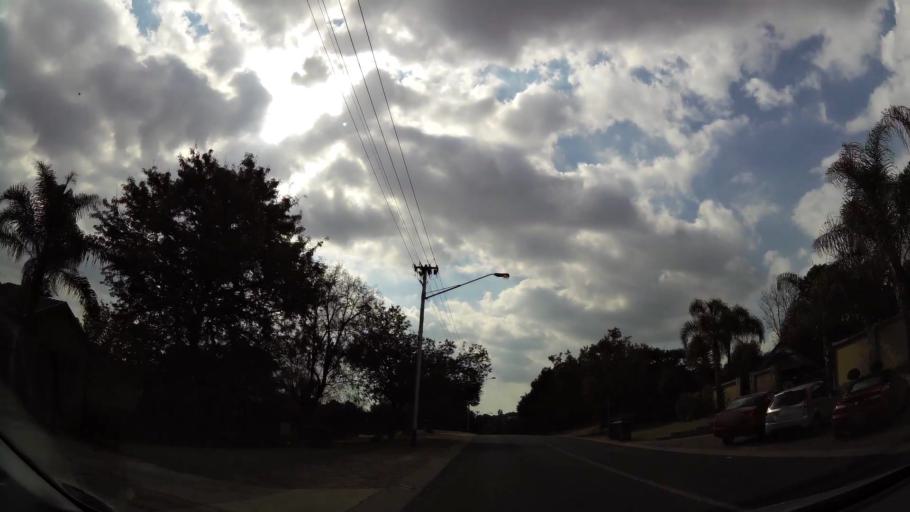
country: ZA
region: Gauteng
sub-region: City of Tshwane Metropolitan Municipality
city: Pretoria
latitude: -25.7628
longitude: 28.2907
